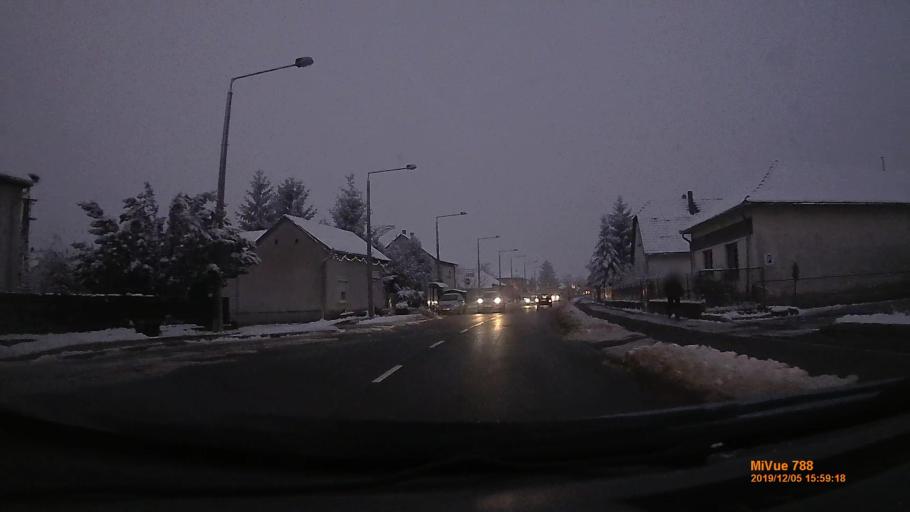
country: HU
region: Borsod-Abauj-Zemplen
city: Tokaj
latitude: 48.1116
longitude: 21.4112
